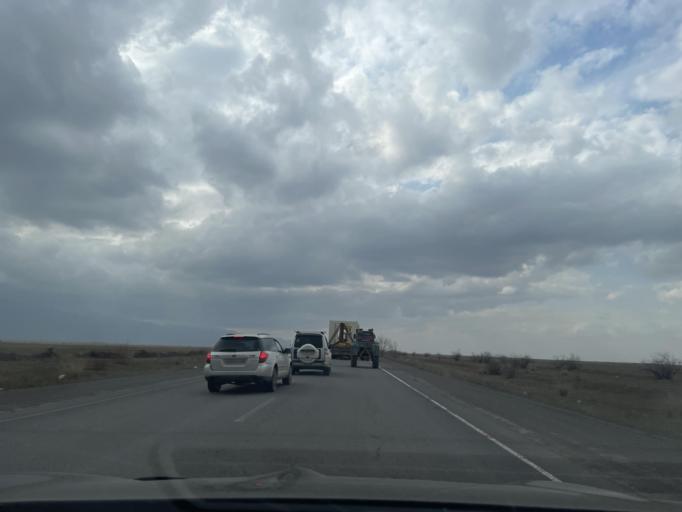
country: KG
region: Chuy
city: Tokmok
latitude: 43.3413
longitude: 75.5537
